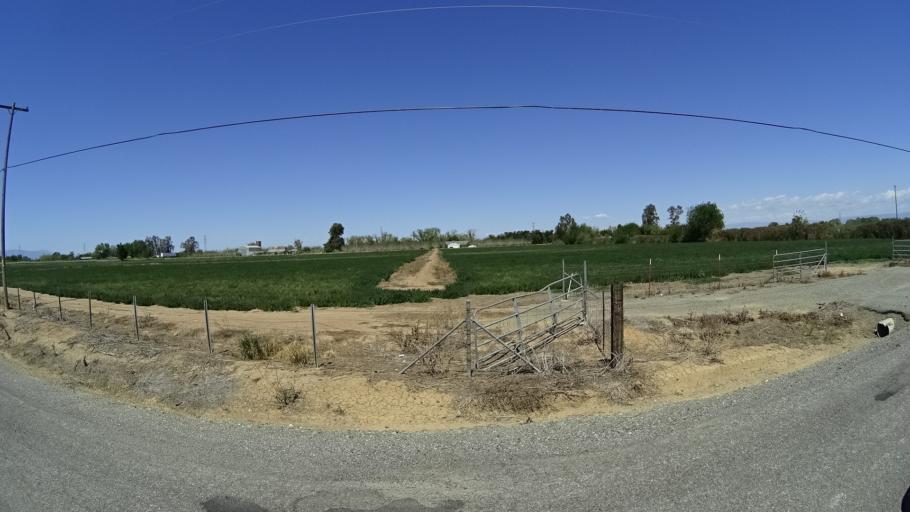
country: US
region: California
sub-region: Glenn County
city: Orland
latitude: 39.7943
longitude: -122.1987
